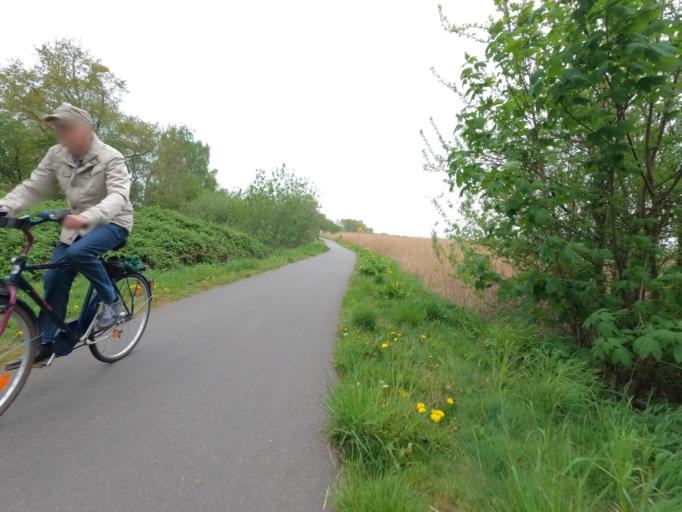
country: DE
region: Mecklenburg-Vorpommern
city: Ribnitz-Damgarten
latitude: 54.2479
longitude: 12.4111
